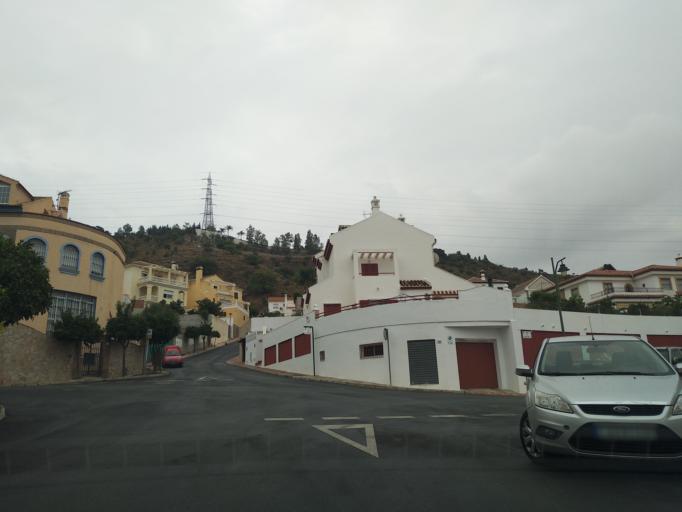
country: ES
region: Andalusia
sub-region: Provincia de Malaga
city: Malaga
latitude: 36.7422
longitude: -4.4766
